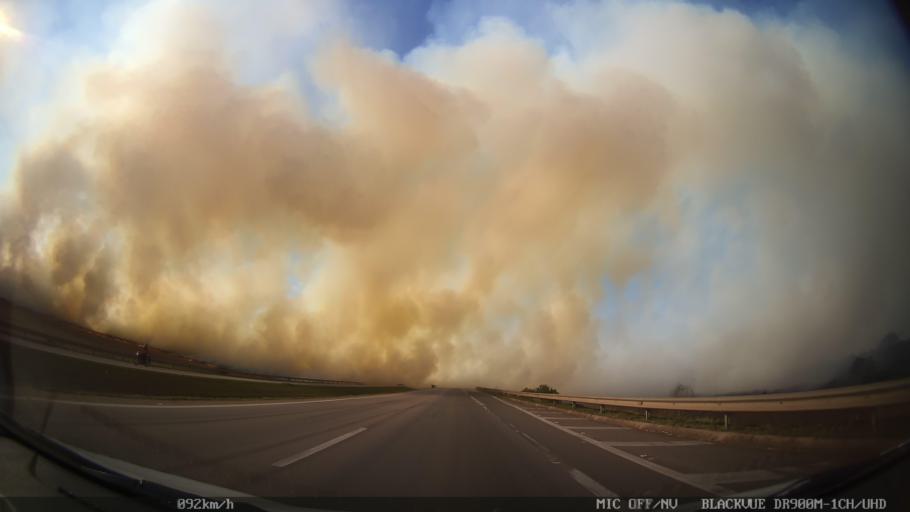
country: BR
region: Sao Paulo
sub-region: Piracicaba
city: Piracicaba
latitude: -22.6966
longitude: -47.6048
